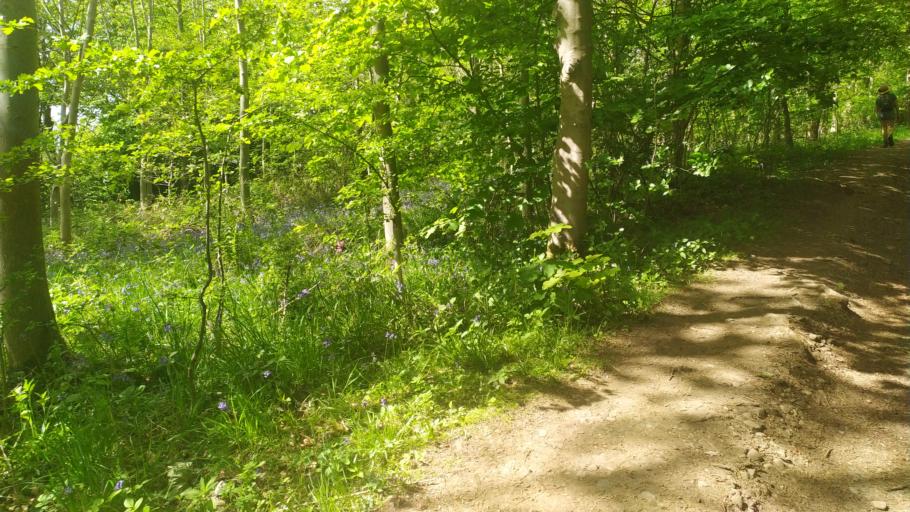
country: GB
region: England
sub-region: City and Borough of Leeds
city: Chapel Allerton
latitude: 53.8865
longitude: -1.5355
